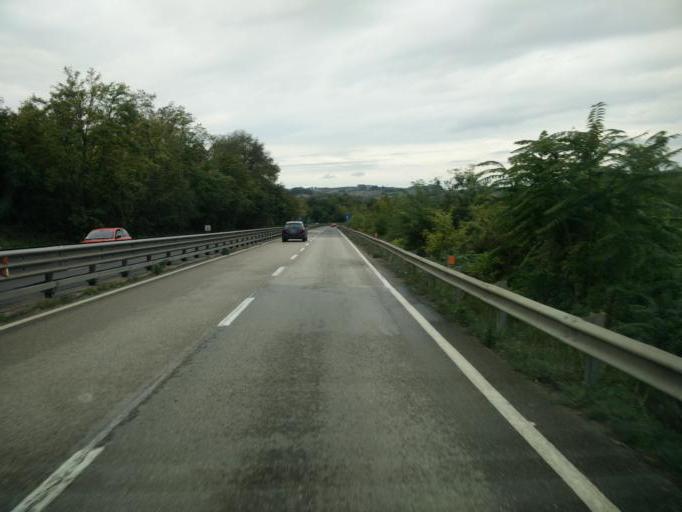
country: IT
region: Tuscany
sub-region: Provincia di Siena
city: Colle di Val d'Elsa
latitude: 43.4227
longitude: 11.1487
